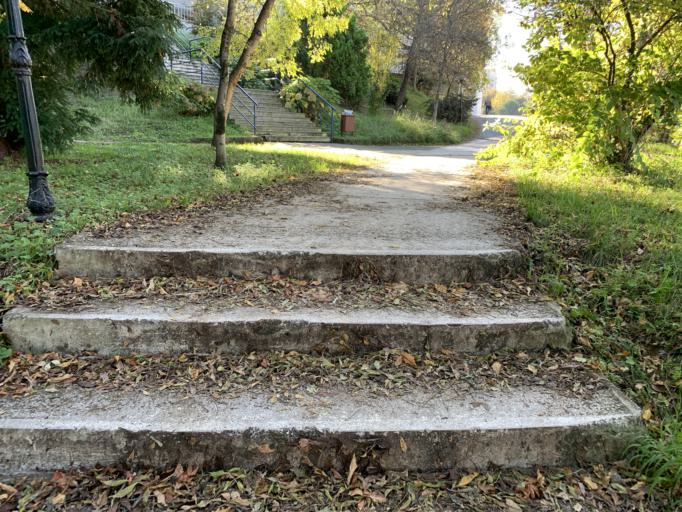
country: TR
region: Trabzon
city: Trabzon
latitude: 40.9957
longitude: 39.7706
